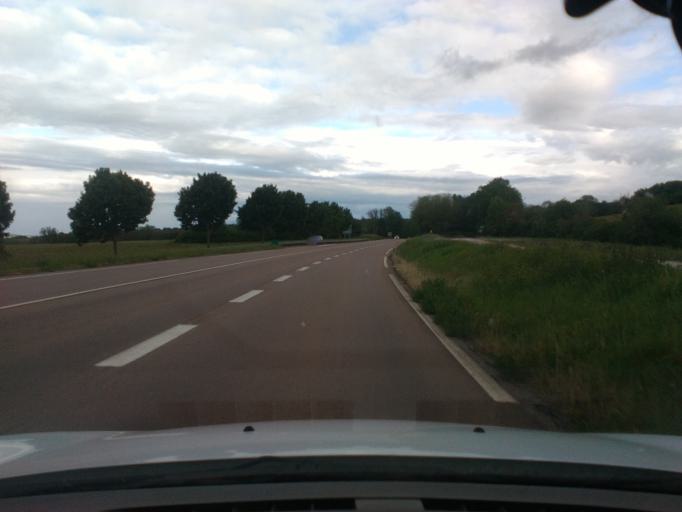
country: FR
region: Lorraine
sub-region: Departement des Vosges
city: Mirecourt
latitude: 48.3084
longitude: 6.0671
